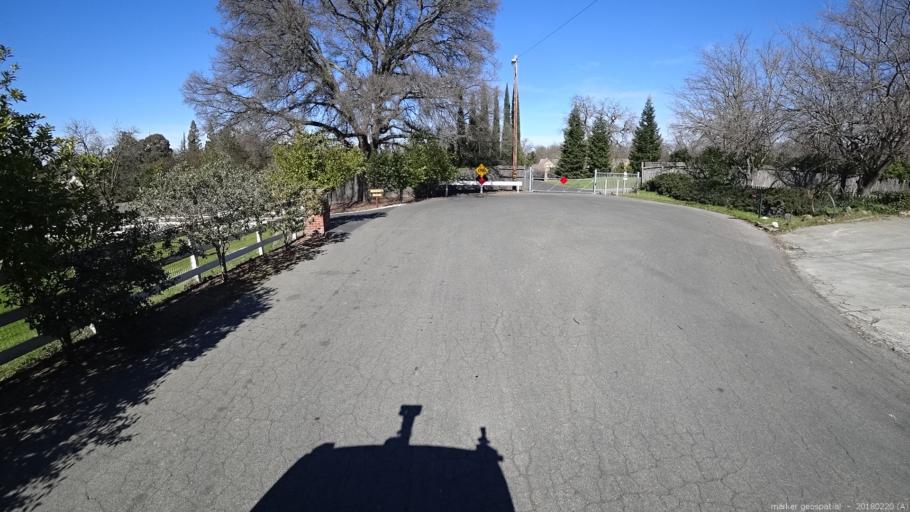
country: US
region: California
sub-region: Sacramento County
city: Orangevale
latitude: 38.7075
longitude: -121.2356
